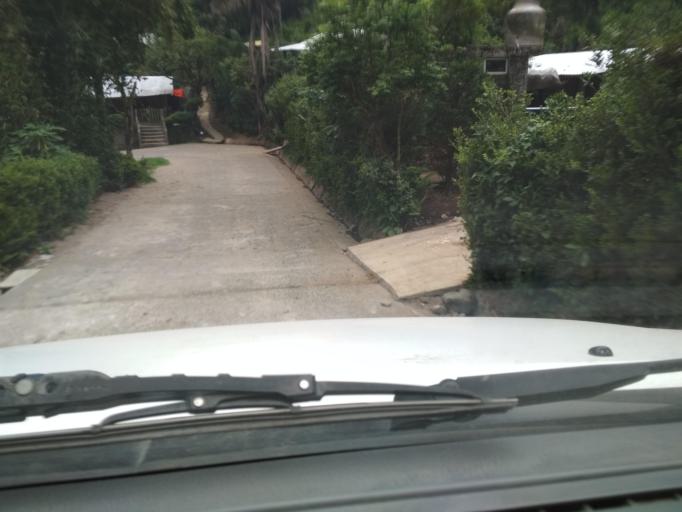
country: MX
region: Veracruz
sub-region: La Perla
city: Barrio de San Miguel
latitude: 18.9295
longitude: -97.1254
